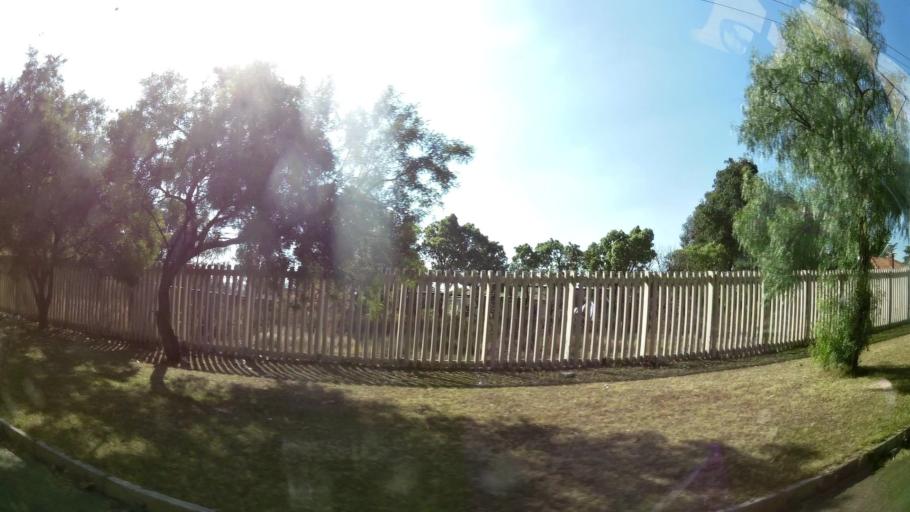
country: ZA
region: Gauteng
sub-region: West Rand District Municipality
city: Randfontein
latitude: -26.1520
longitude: 27.6973
